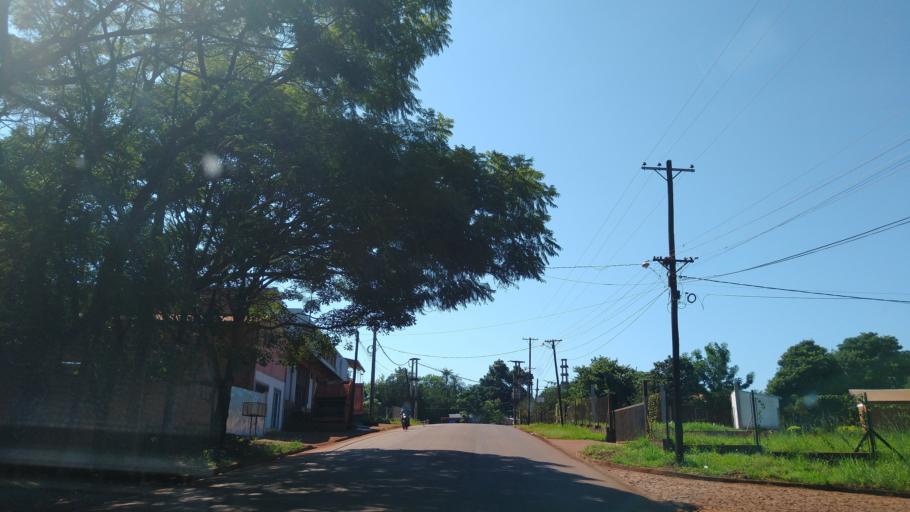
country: AR
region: Misiones
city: Puerto Libertad
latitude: -25.9772
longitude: -54.5730
